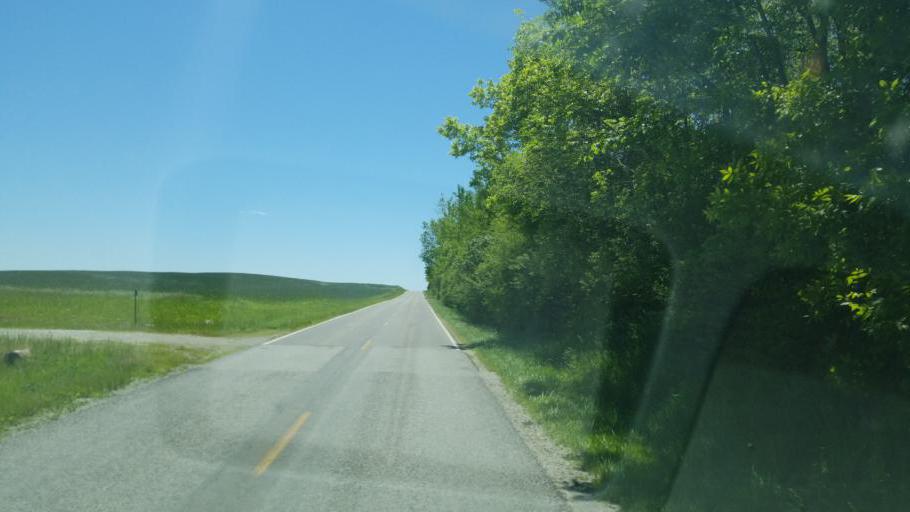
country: US
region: Ohio
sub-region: Mercer County
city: Fort Recovery
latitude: 40.3204
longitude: -84.8035
